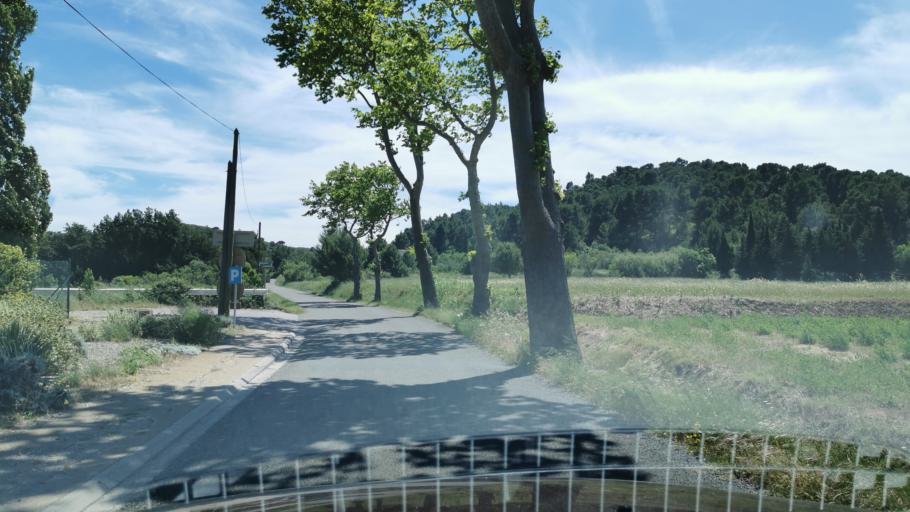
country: FR
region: Languedoc-Roussillon
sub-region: Departement de l'Aude
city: Nevian
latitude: 43.2075
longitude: 2.9033
